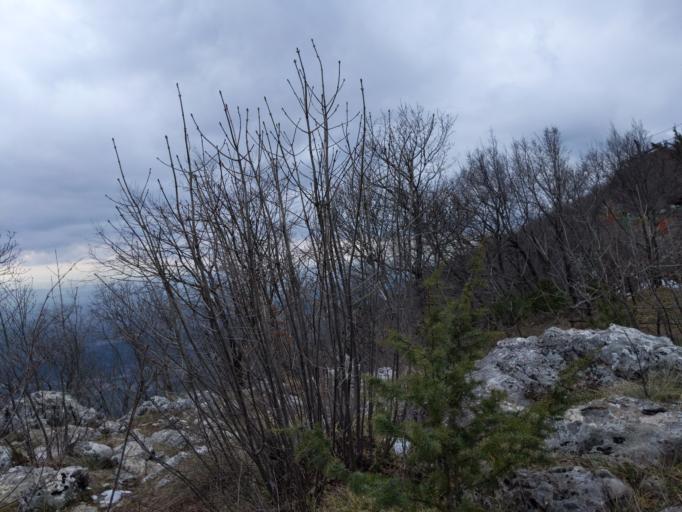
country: AL
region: Tirane
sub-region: Rrethi i Tiranes
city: Dajt
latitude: 41.3675
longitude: 19.9055
